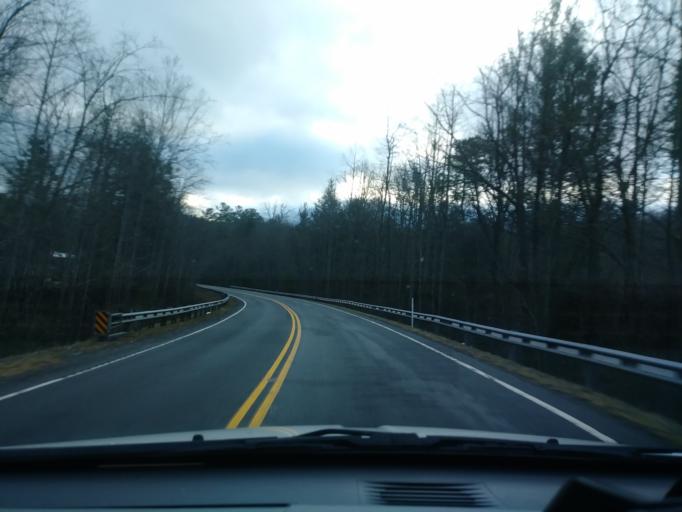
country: US
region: Tennessee
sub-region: Unicoi County
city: Unicoi
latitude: 36.1743
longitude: -82.3127
